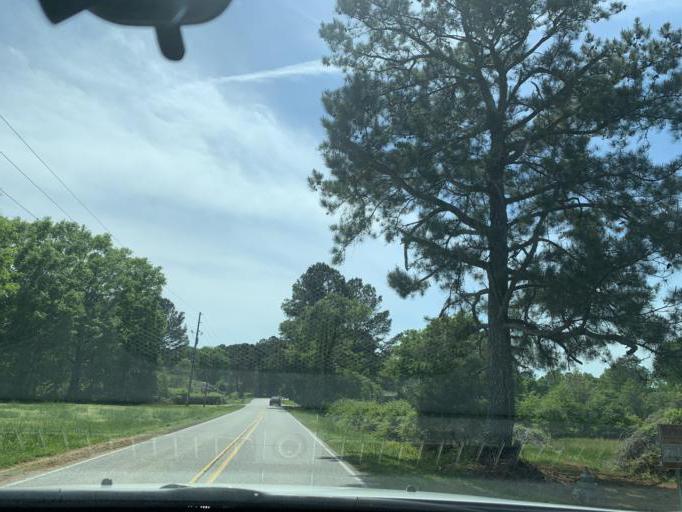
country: US
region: Georgia
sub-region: Forsyth County
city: Cumming
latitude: 34.2741
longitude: -84.1851
